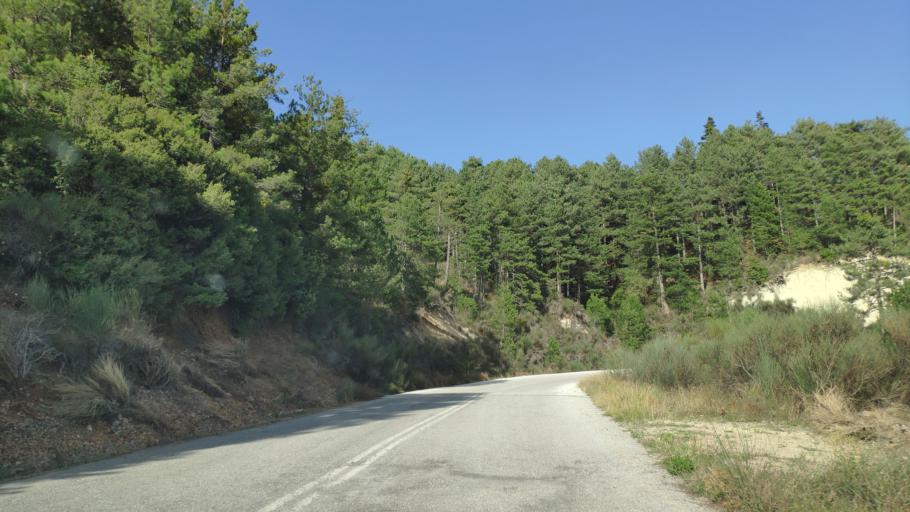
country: GR
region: West Greece
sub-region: Nomos Achaias
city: Aiyira
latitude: 38.0037
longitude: 22.3927
